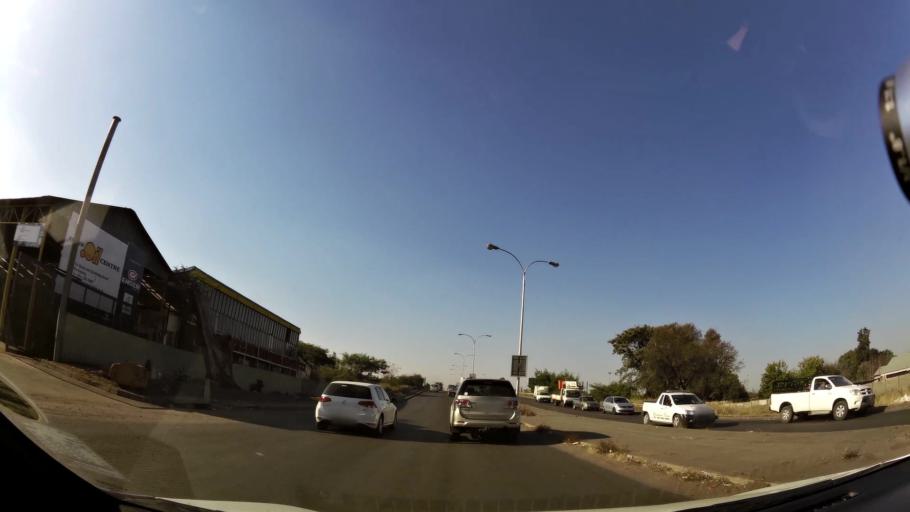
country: ZA
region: North-West
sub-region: Bojanala Platinum District Municipality
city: Rustenburg
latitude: -25.6709
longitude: 27.2544
